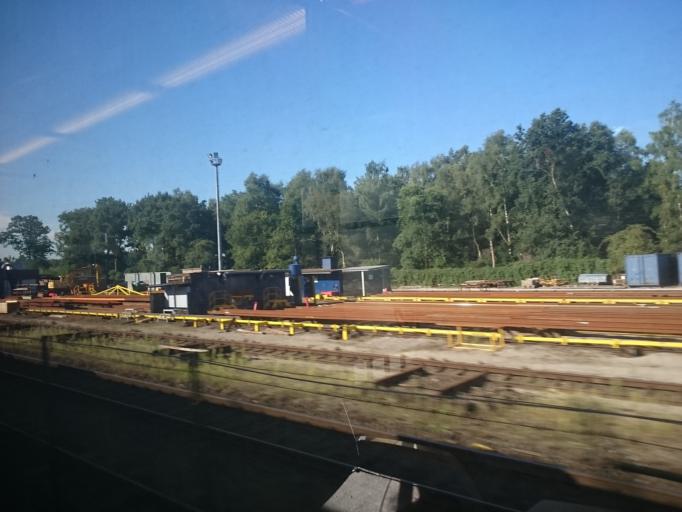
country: DE
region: North Rhine-Westphalia
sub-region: Regierungsbezirk Dusseldorf
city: Ratingen
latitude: 51.3634
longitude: 6.8166
